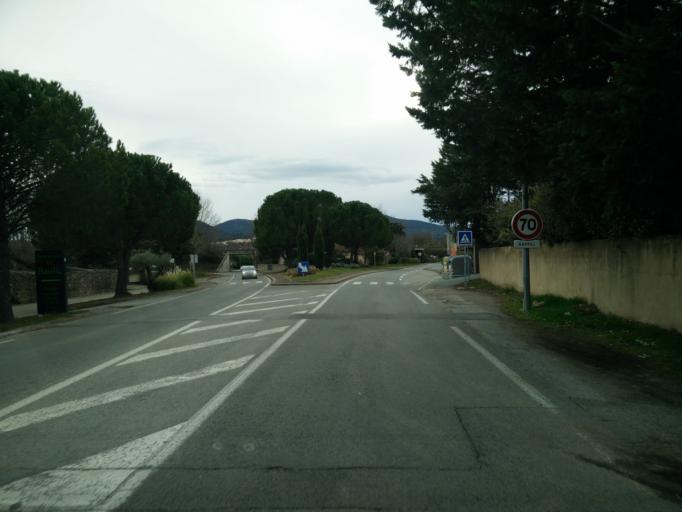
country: FR
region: Provence-Alpes-Cote d'Azur
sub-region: Departement du Var
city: Roquebrune-sur-Argens
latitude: 43.4583
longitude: 6.6349
